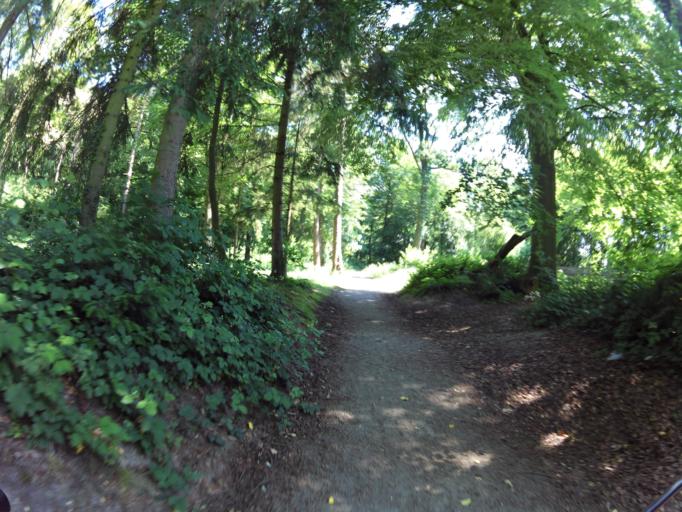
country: NL
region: Limburg
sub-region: Gemeente Kerkrade
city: Kerkrade
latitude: 50.8704
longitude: 6.0555
